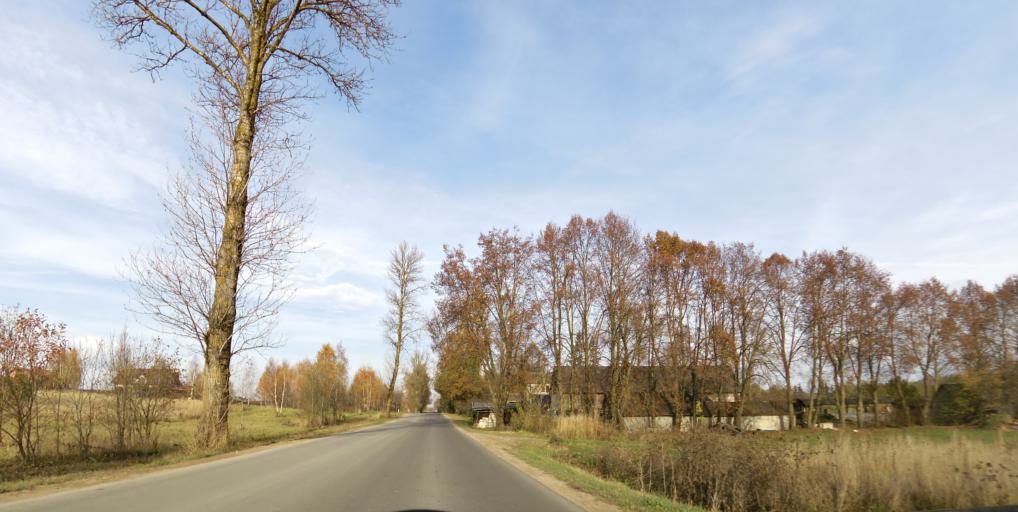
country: LT
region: Vilnius County
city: Pilaite
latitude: 54.7136
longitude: 25.1602
